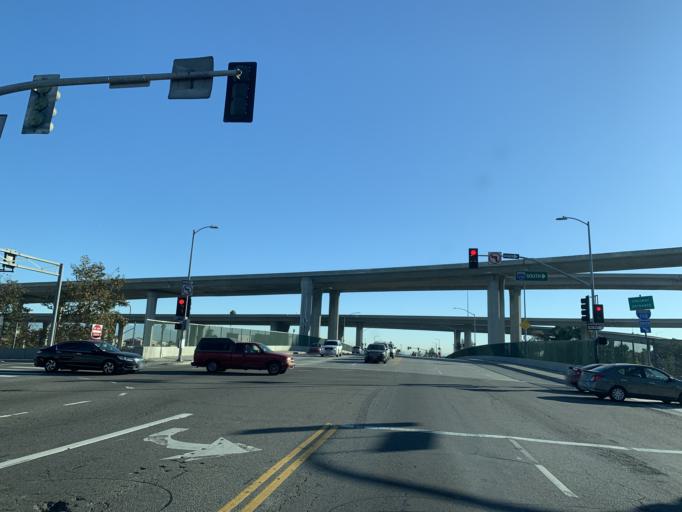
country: US
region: California
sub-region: Los Angeles County
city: West Athens
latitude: 33.9310
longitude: -118.2820
